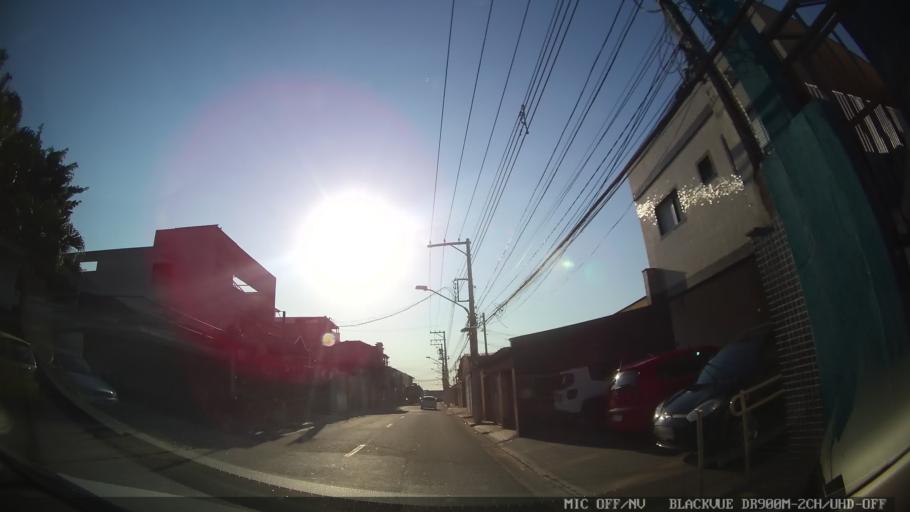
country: BR
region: Sao Paulo
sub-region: Sao Paulo
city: Sao Paulo
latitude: -23.4957
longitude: -46.6391
